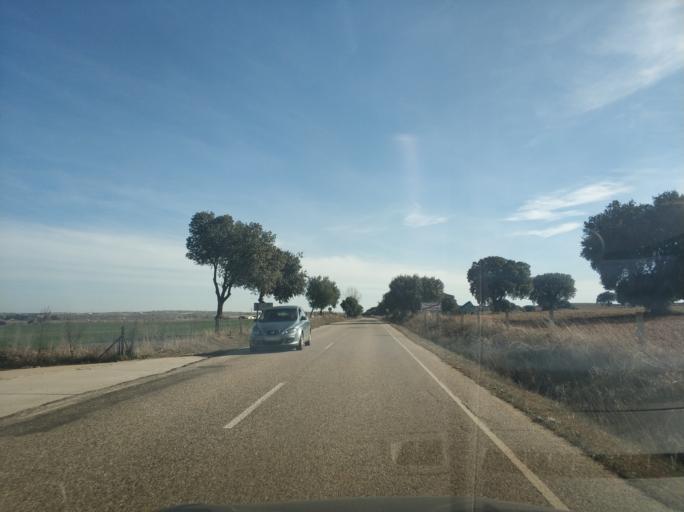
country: ES
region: Castille and Leon
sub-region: Provincia de Salamanca
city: Florida de Liebana
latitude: 41.0165
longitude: -5.7432
